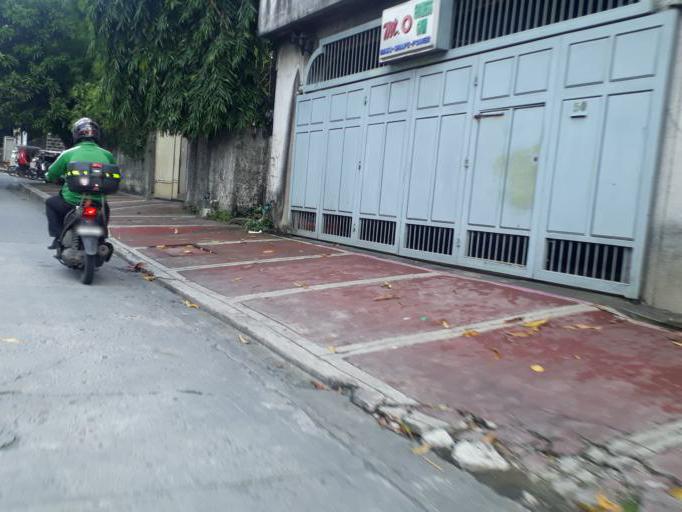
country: PH
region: Metro Manila
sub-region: Quezon City
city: Quezon City
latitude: 14.6356
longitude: 121.0680
